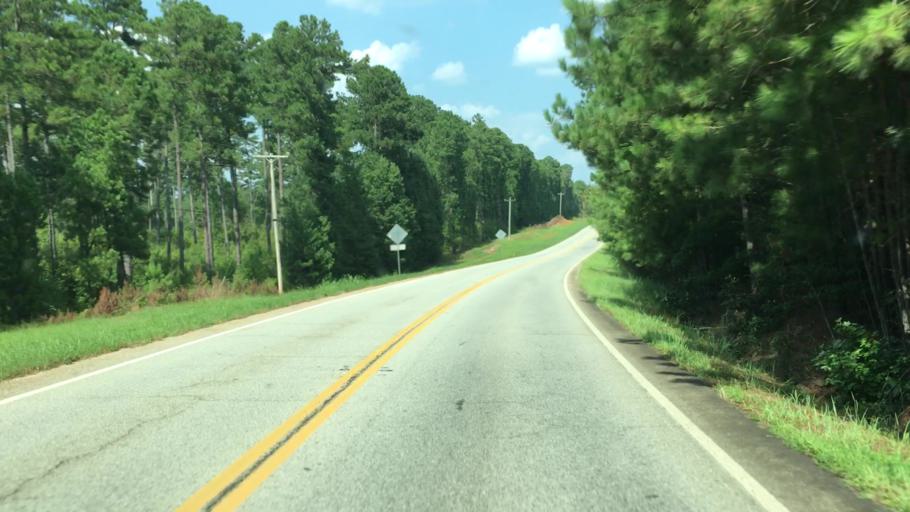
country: US
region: Georgia
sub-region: Monroe County
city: Forsyth
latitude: 33.1330
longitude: -83.8695
